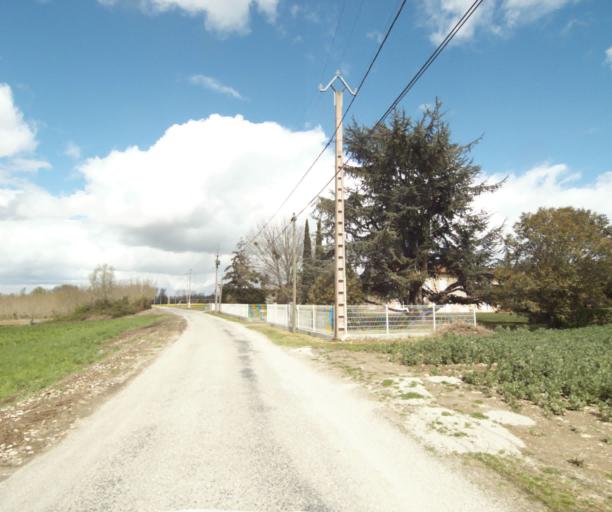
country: FR
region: Midi-Pyrenees
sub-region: Departement de l'Ariege
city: Saverdun
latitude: 43.2442
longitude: 1.5828
